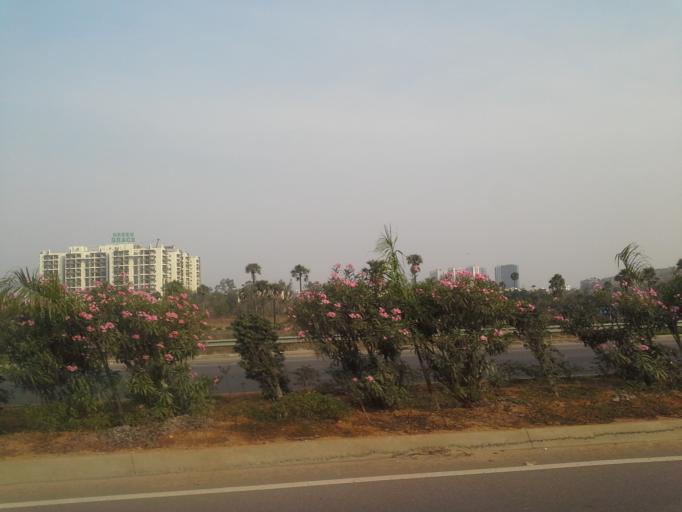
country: IN
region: Telangana
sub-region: Rangareddi
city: Kukatpalli
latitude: 17.4205
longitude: 78.3566
